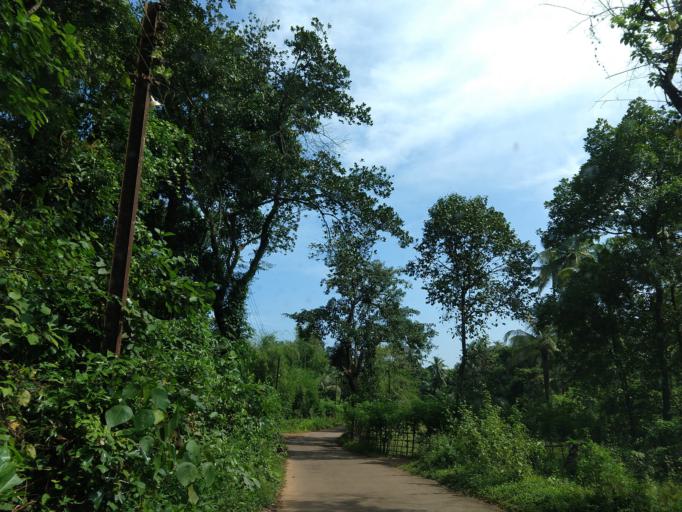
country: IN
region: Maharashtra
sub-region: Sindhudurg
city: Kudal
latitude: 16.0411
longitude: 73.6833
